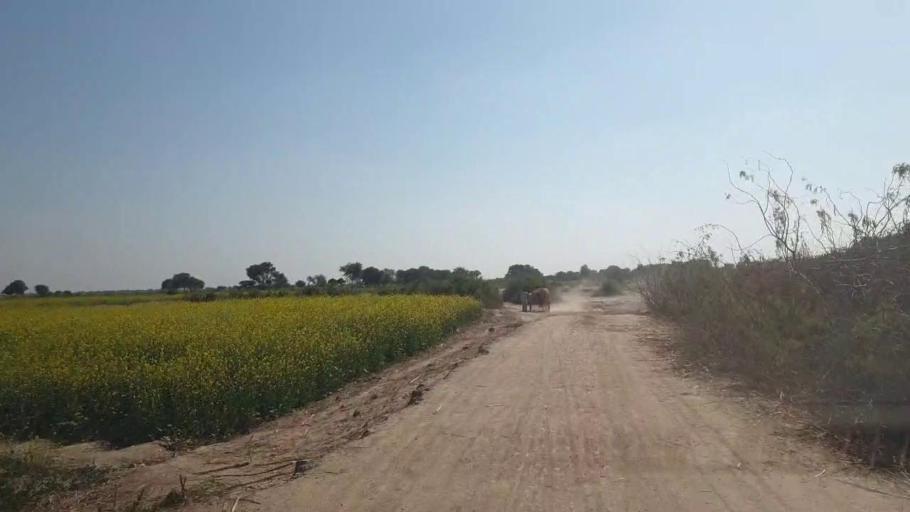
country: PK
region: Sindh
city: Chambar
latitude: 25.3101
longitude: 68.7208
